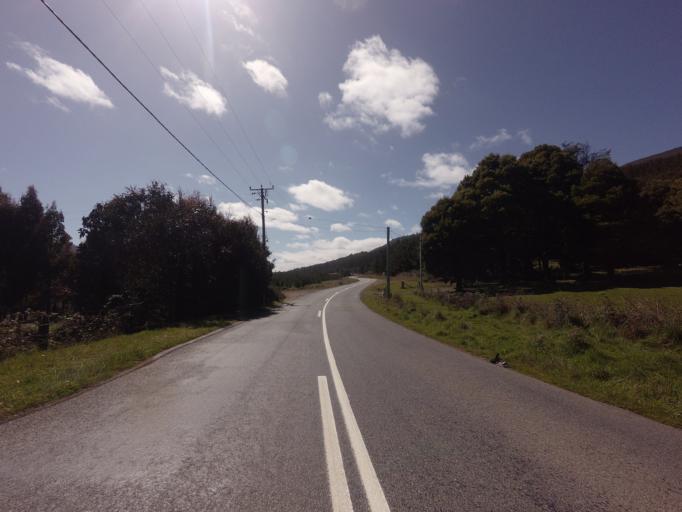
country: AU
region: Tasmania
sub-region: Derwent Valley
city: New Norfolk
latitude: -42.7473
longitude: 146.6496
